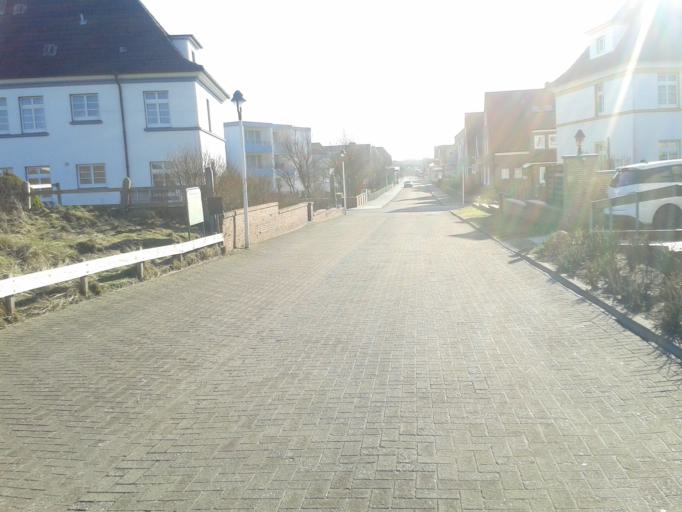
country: DE
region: Lower Saxony
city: Norderney
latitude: 53.7116
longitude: 7.1507
